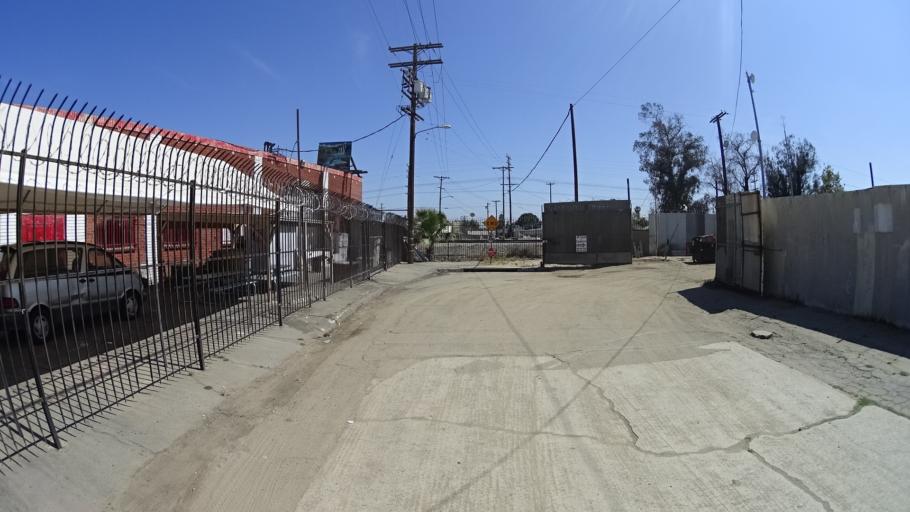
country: US
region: California
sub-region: Los Angeles County
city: Van Nuys
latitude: 34.2083
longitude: -118.4288
